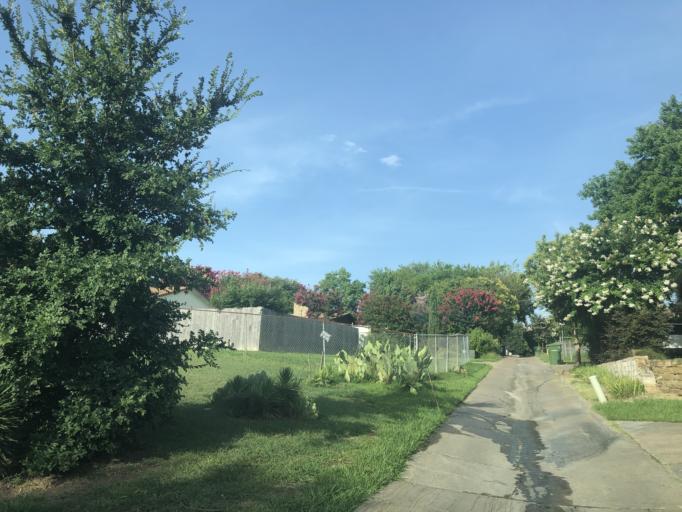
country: US
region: Texas
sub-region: Dallas County
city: Sunnyvale
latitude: 32.8394
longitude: -96.5814
